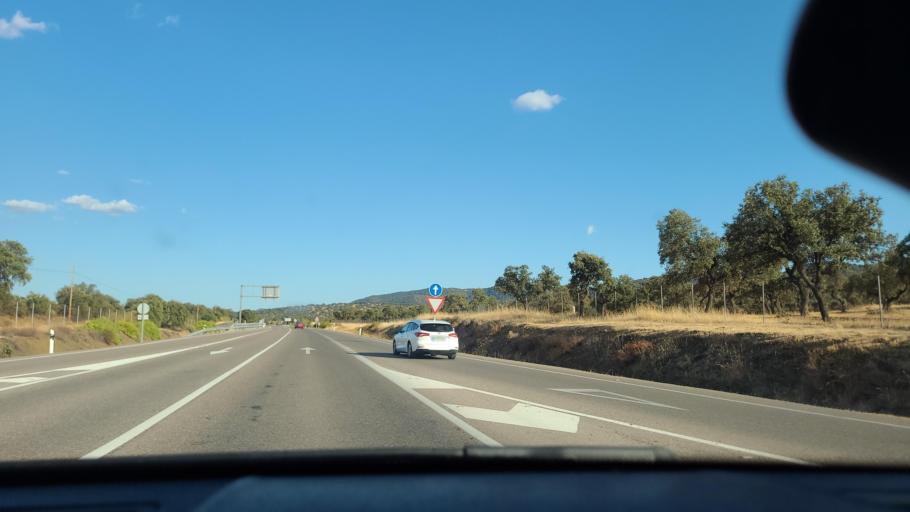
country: ES
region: Andalusia
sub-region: Province of Cordoba
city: Belmez
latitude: 38.2129
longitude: -5.1390
